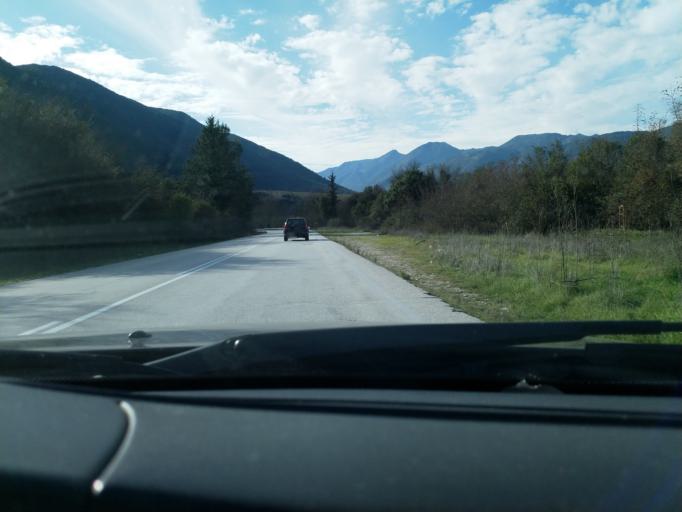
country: GR
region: Epirus
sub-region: Nomos Ioanninon
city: Agia Kyriaki
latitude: 39.4581
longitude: 20.8777
